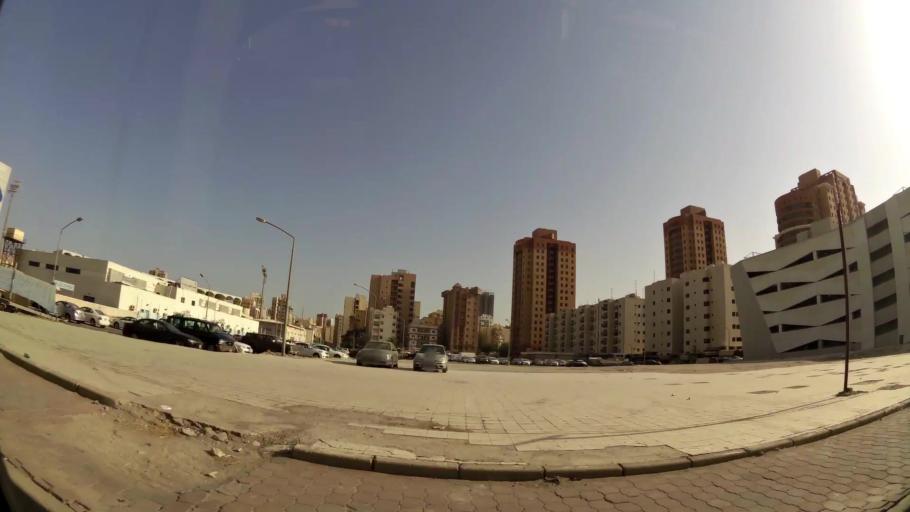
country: KW
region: Muhafazat Hawalli
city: As Salimiyah
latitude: 29.3417
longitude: 48.0863
